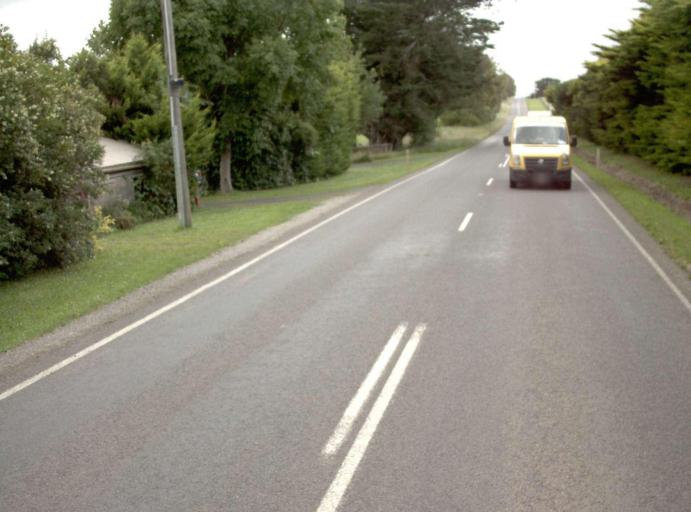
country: AU
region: Victoria
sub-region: Baw Baw
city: Warragul
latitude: -38.1190
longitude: 145.9805
